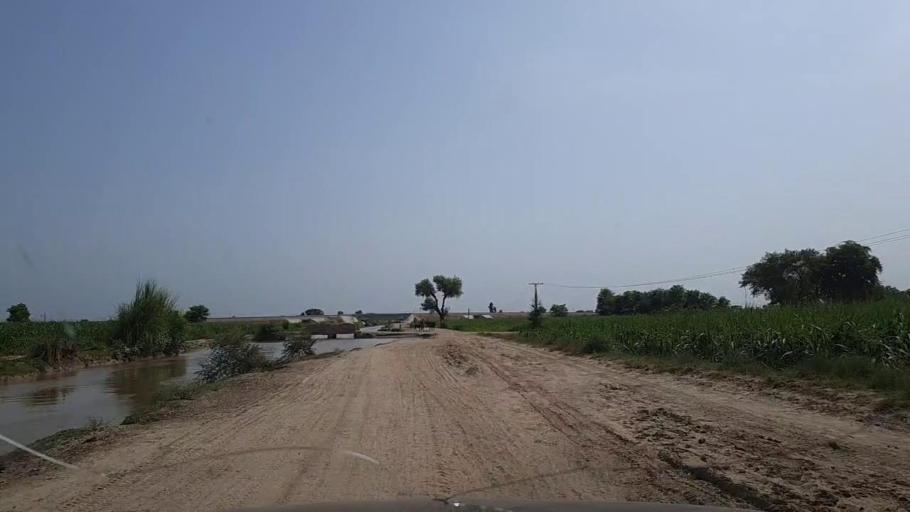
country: PK
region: Sindh
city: Ghotki
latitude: 28.0663
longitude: 69.3836
